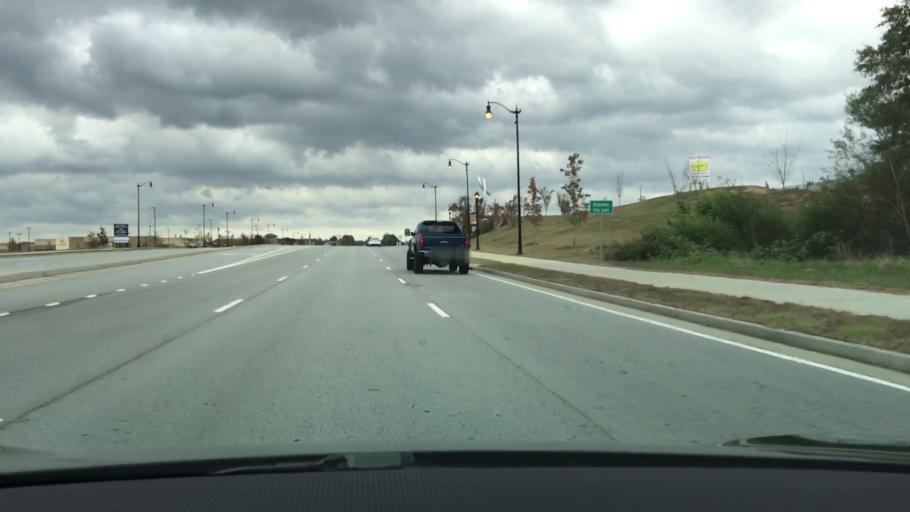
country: US
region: Georgia
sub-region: Jackson County
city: Braselton
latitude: 34.1199
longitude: -83.8327
